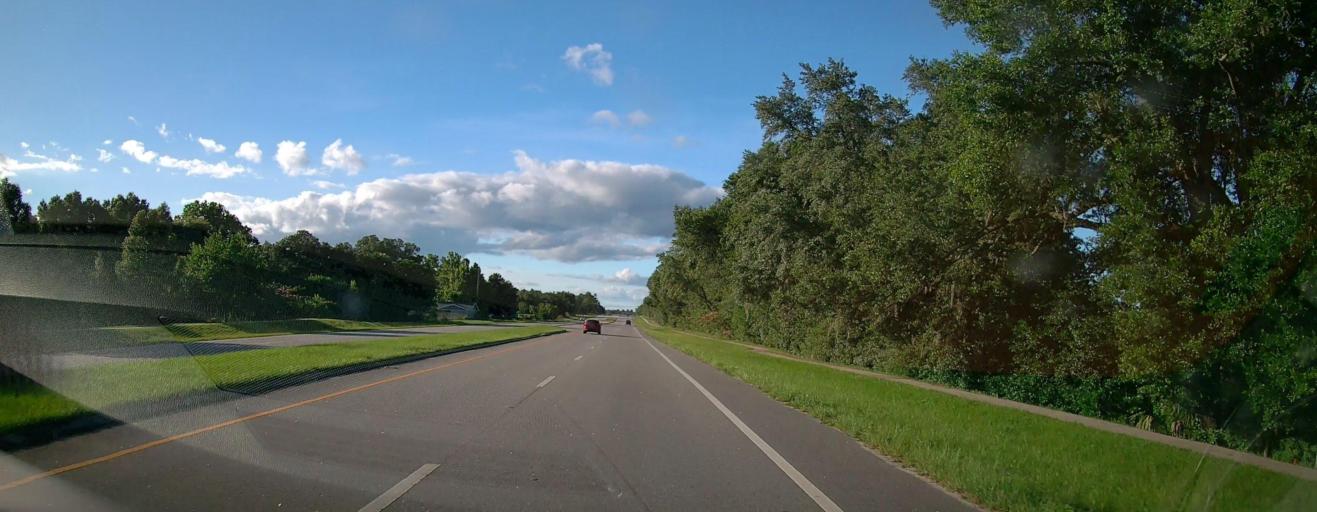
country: US
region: Florida
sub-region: Marion County
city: Belleview
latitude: 29.0363
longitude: -82.0176
